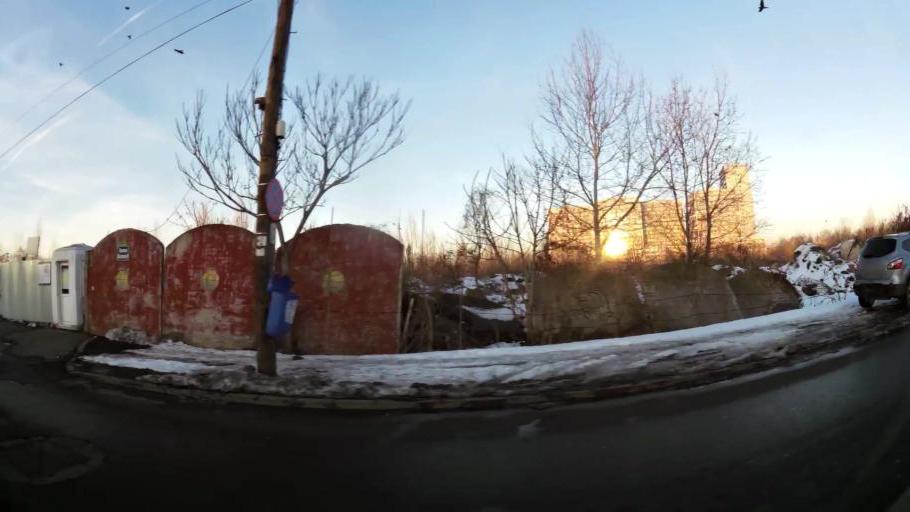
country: RO
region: Ilfov
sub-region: Comuna Fundeni-Dobroesti
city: Fundeni
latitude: 44.4499
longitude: 26.1415
